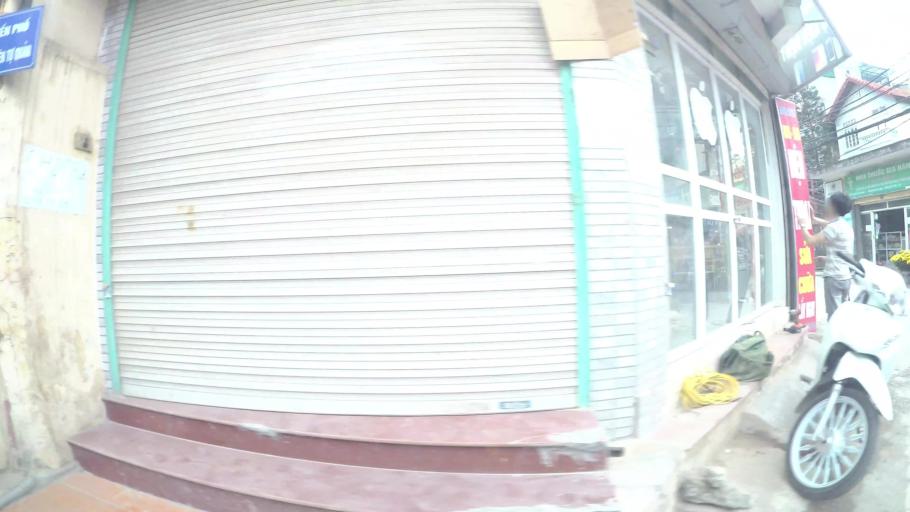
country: VN
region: Ha Noi
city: Hai BaTrung
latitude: 20.9933
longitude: 105.8888
